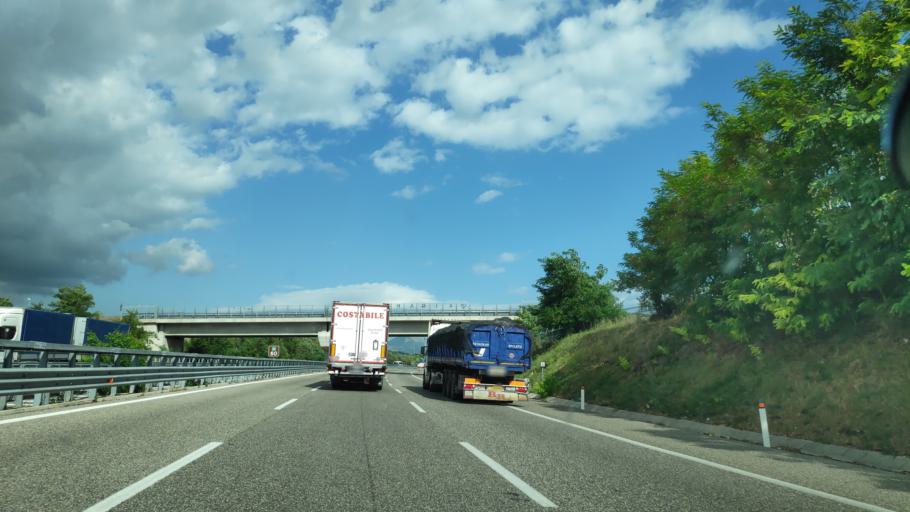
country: IT
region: Campania
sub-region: Provincia di Salerno
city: Contursi Terme
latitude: 40.6145
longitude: 15.2745
